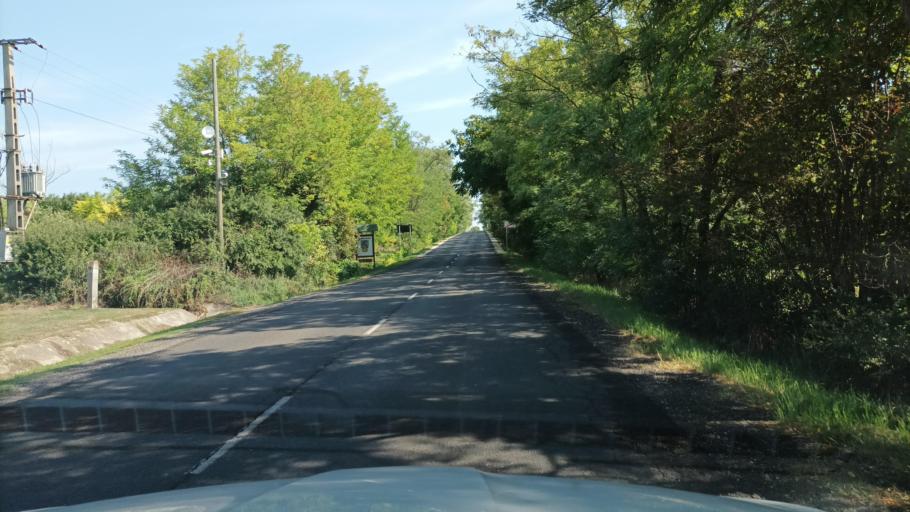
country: HU
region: Pest
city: Valko
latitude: 47.5675
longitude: 19.5222
